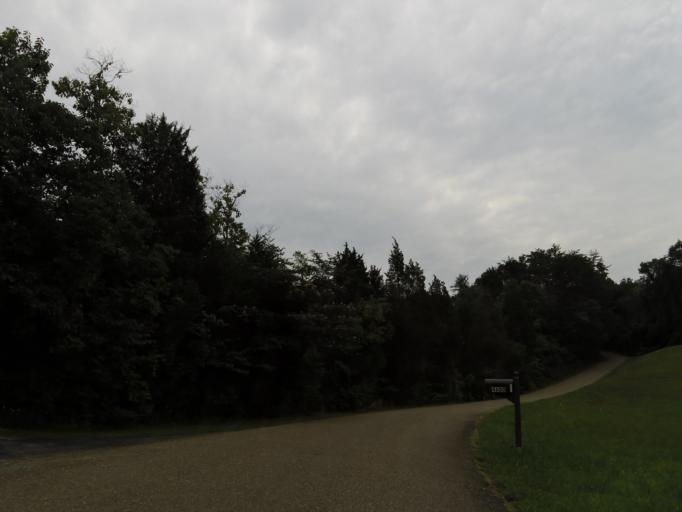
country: US
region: Tennessee
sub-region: Sevier County
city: Seymour
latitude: 35.9419
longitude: -83.7962
